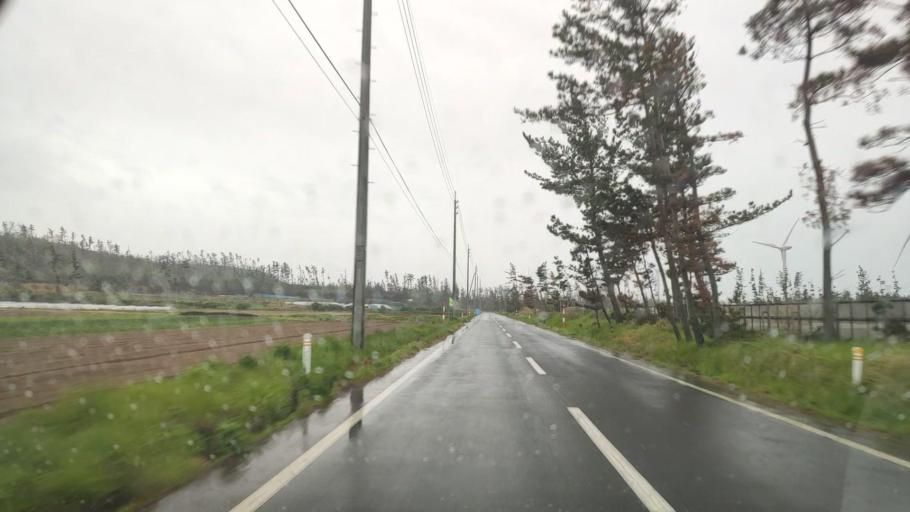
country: JP
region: Akita
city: Noshiromachi
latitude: 40.0837
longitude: 139.9568
